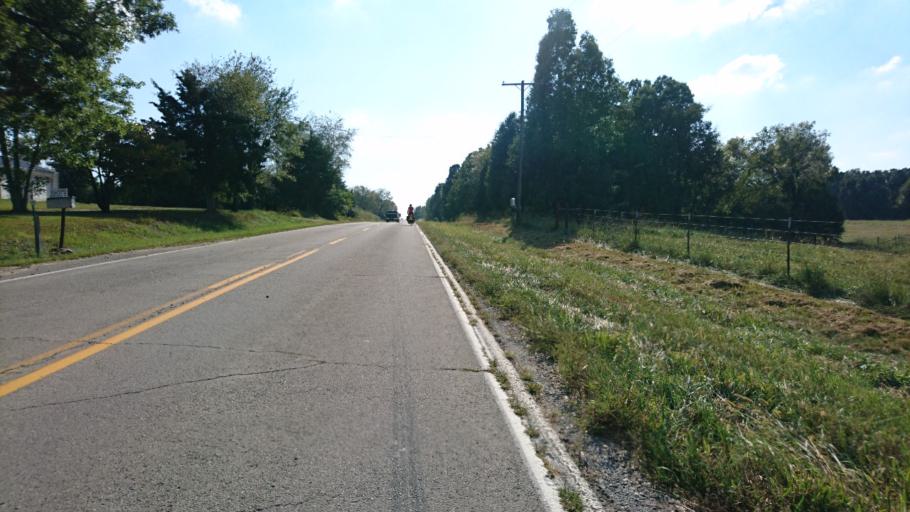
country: US
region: Missouri
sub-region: Laclede County
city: Lebanon
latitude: 37.6088
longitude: -92.7035
